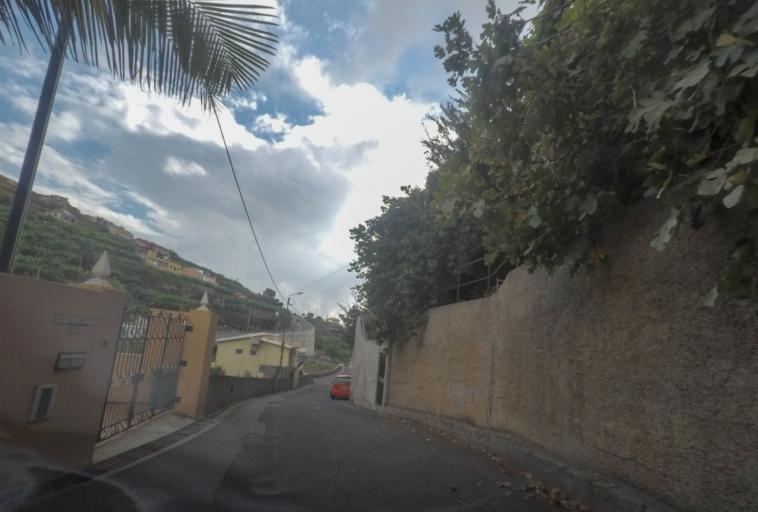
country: PT
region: Madeira
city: Camara de Lobos
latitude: 32.6538
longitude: -16.9591
